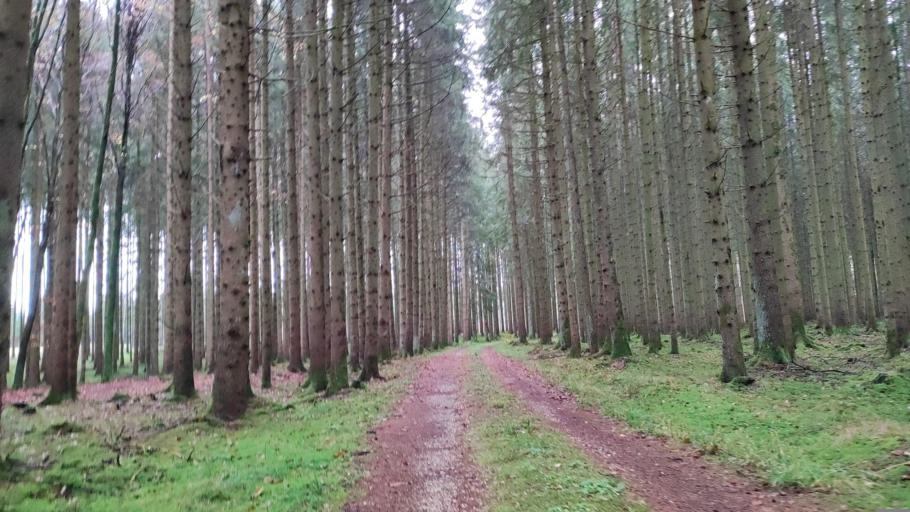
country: DE
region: Bavaria
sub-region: Swabia
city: Landensberg
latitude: 48.3659
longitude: 10.5178
